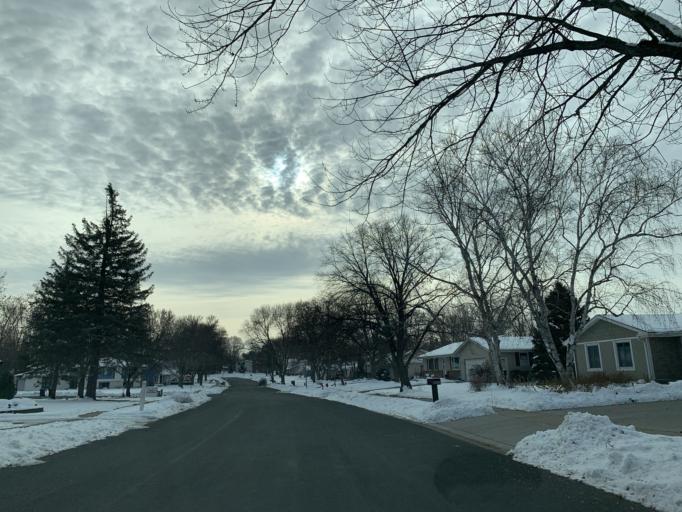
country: US
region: Minnesota
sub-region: Scott County
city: Savage
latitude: 44.8320
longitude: -93.3548
